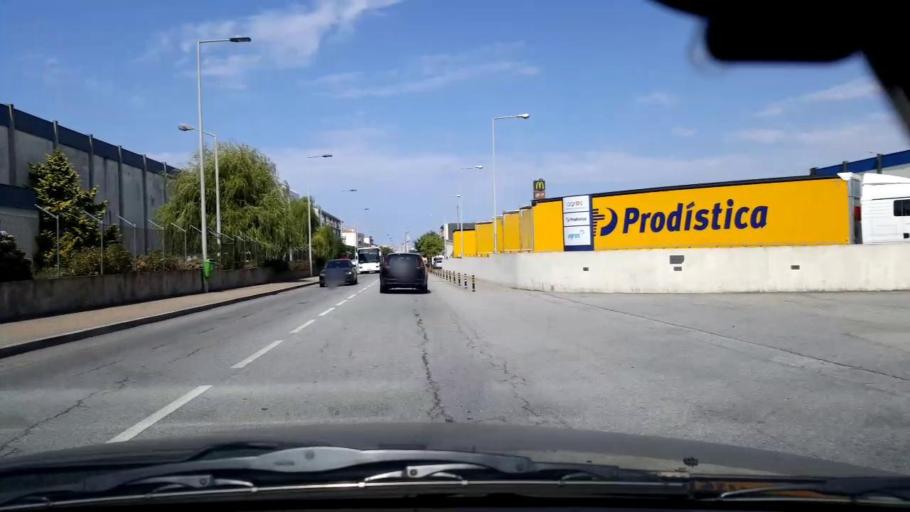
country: PT
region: Porto
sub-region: Vila do Conde
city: Vila do Conde
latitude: 41.3664
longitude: -8.7495
